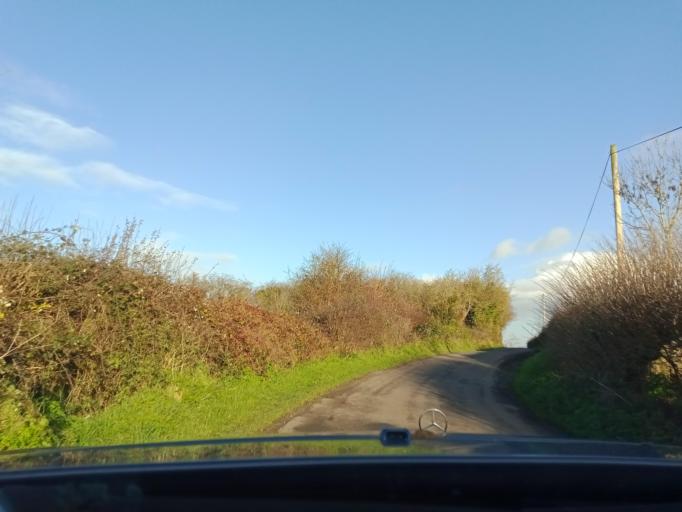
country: IE
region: Leinster
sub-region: Kilkenny
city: Callan
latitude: 52.4976
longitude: -7.3567
